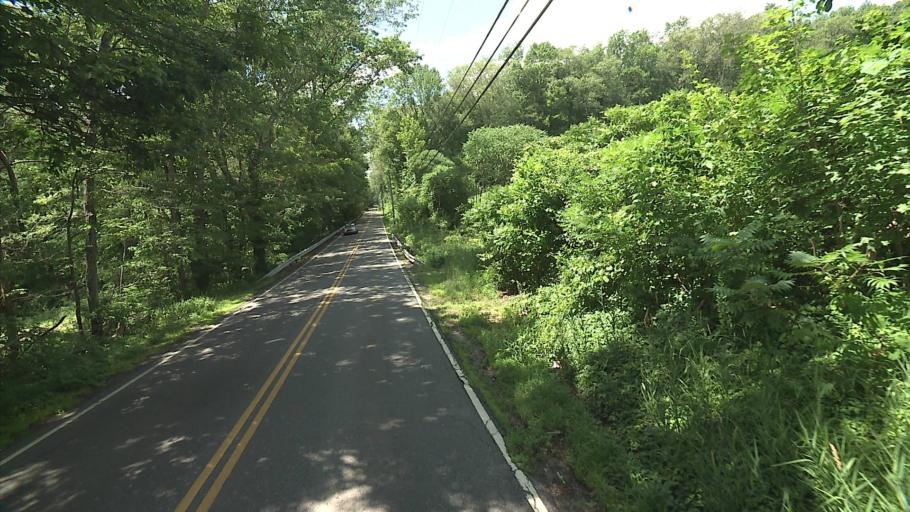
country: US
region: Massachusetts
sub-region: Worcester County
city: Southbridge
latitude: 41.9723
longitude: -72.0632
